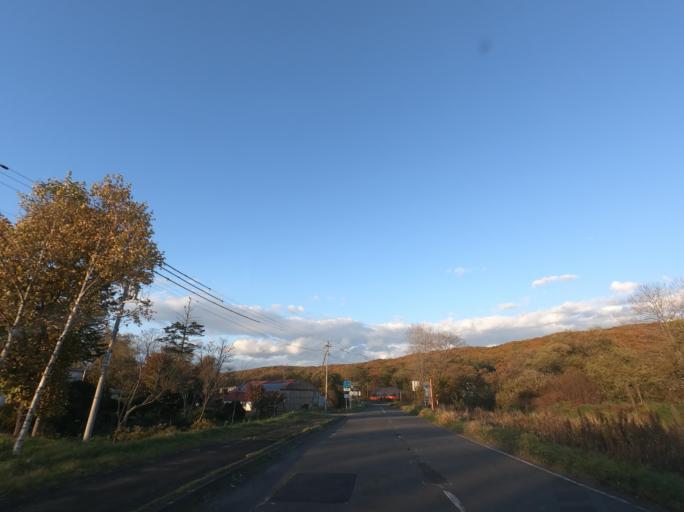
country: JP
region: Hokkaido
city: Kushiro
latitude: 43.2253
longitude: 144.4346
